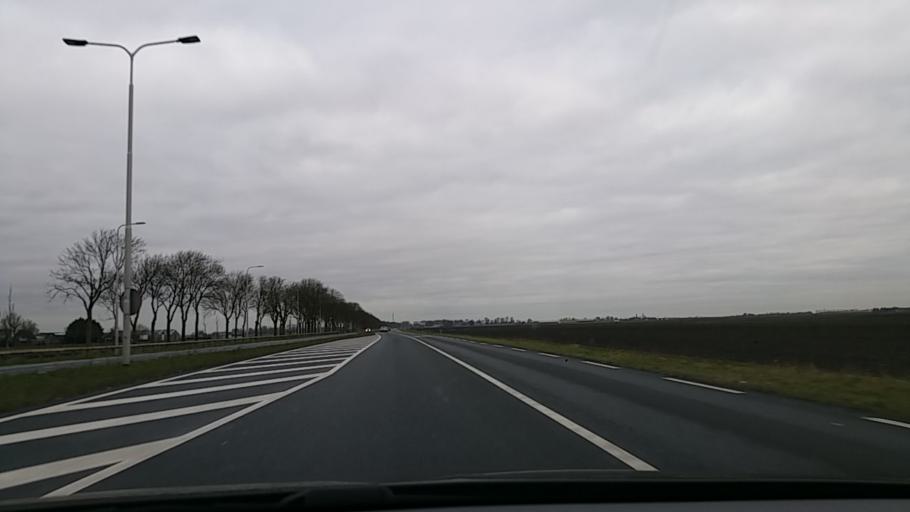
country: NL
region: South Holland
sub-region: Gemeente Alphen aan den Rijn
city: Alphen aan den Rijn
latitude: 52.1703
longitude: 4.6687
